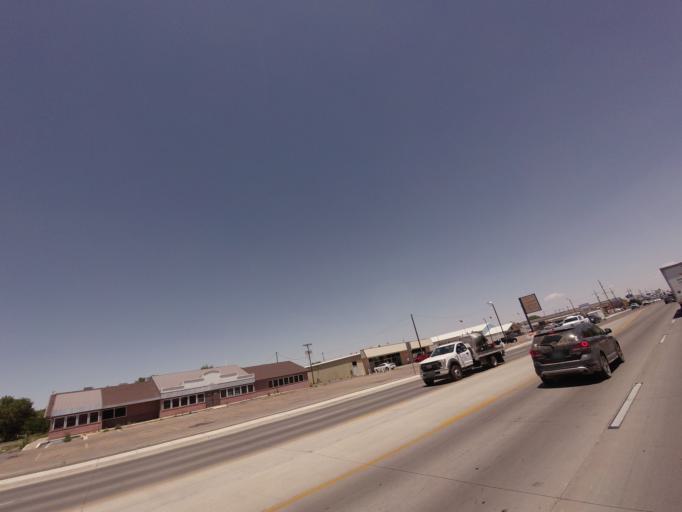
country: US
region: New Mexico
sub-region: Curry County
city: Clovis
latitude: 34.3964
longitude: -103.1807
